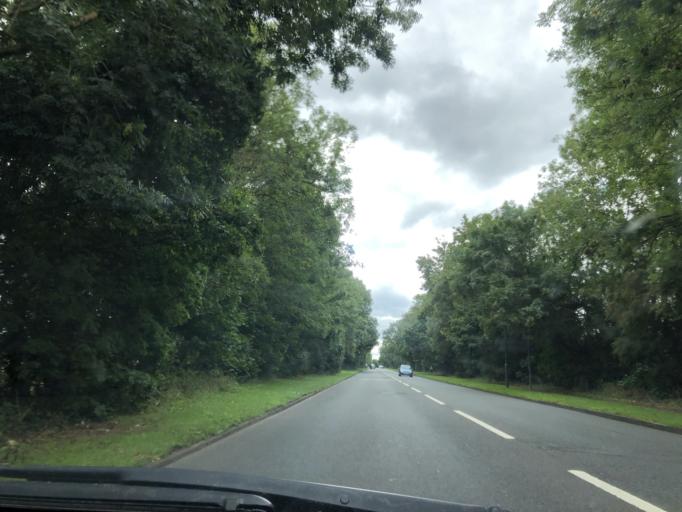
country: GB
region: England
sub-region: Kent
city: Halstead
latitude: 51.3553
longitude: 0.1265
